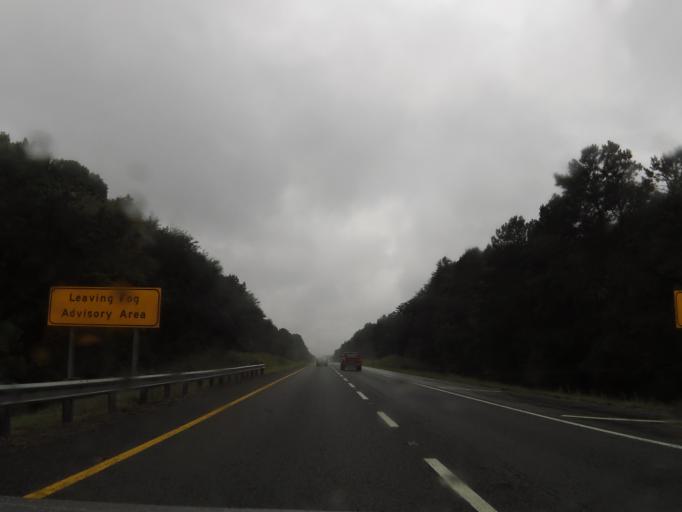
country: US
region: Tennessee
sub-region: Bradley County
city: Hopewell
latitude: 35.2684
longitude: -84.8280
